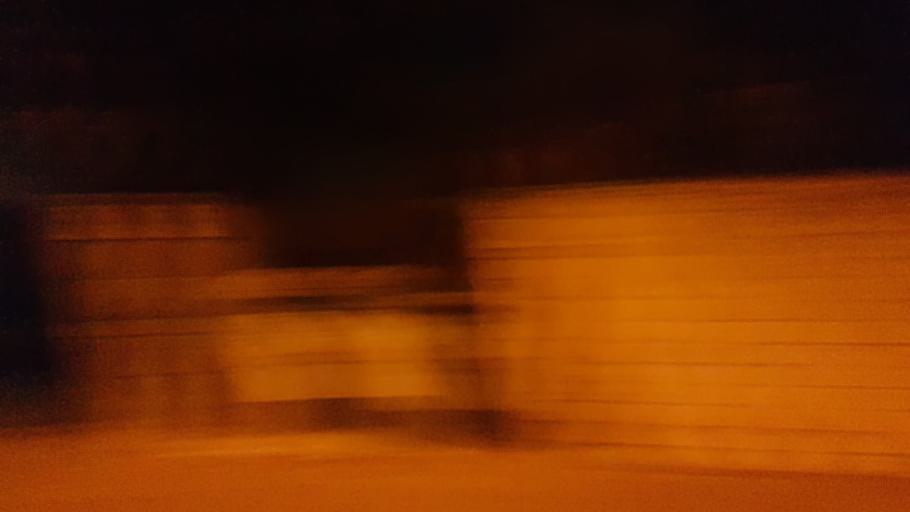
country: IL
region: Central District
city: Hod HaSharon
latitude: 32.1646
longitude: 34.8939
